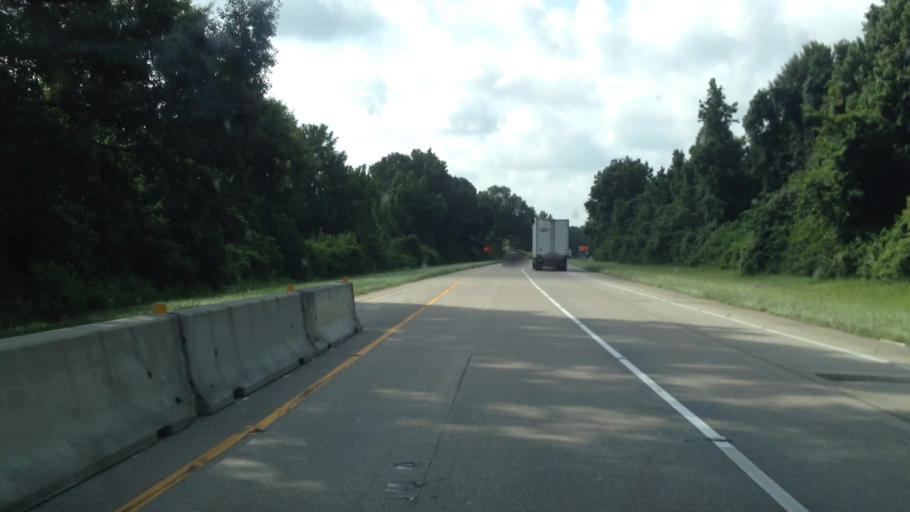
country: US
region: Louisiana
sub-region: Ascension Parish
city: Prairieville
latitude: 30.3144
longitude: -90.9987
